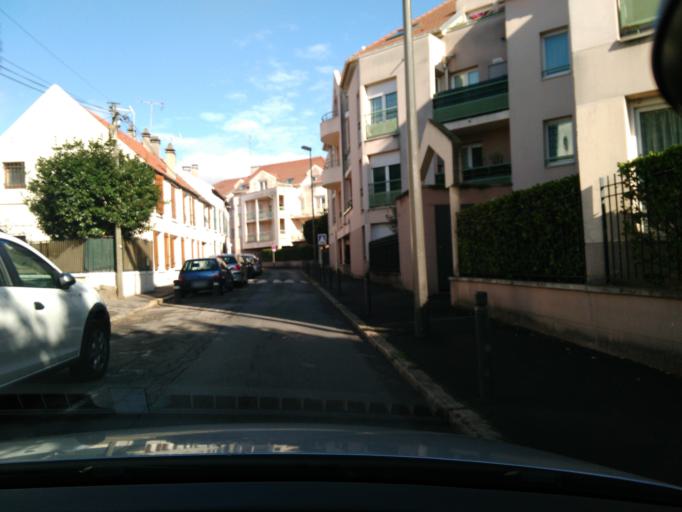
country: FR
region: Ile-de-France
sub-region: Departement de l'Essonne
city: Massy
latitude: 48.7287
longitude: 2.2786
